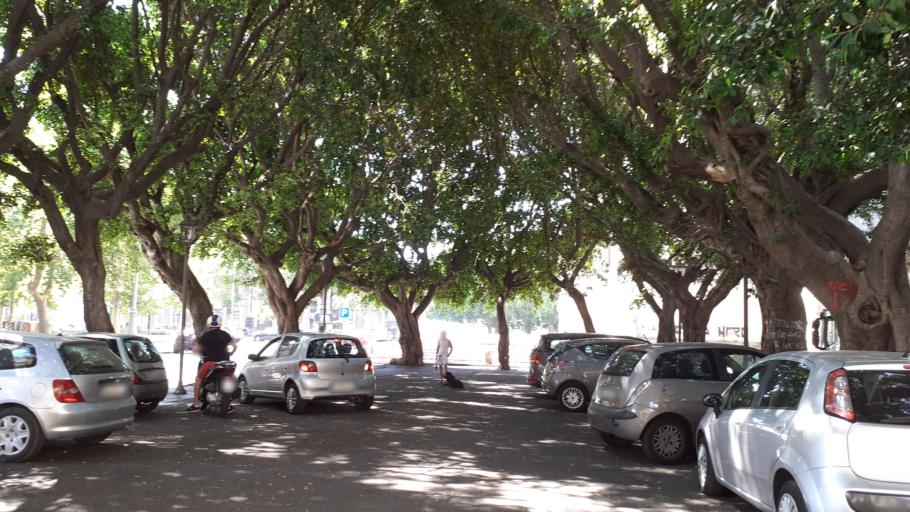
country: IT
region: Sicily
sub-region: Catania
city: Catania
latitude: 37.5048
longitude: 15.0807
